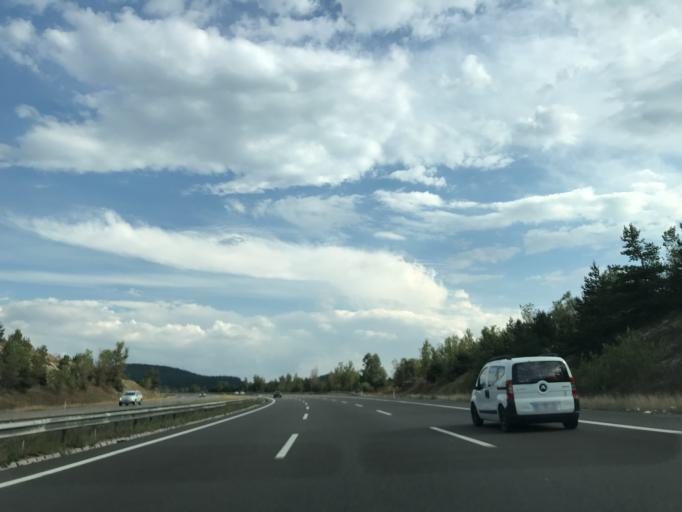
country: TR
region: Bolu
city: Gerede
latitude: 40.6414
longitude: 32.2306
